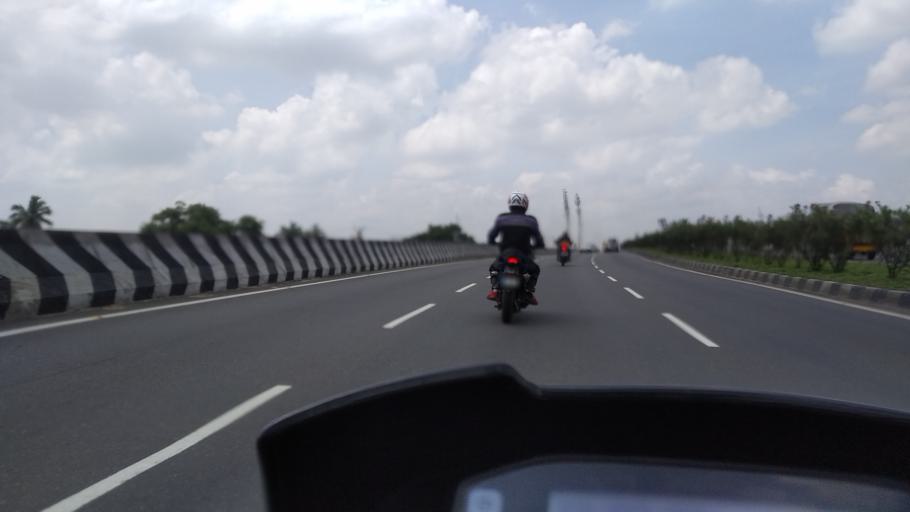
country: IN
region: Tamil Nadu
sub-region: Tiruppur
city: Avinashi
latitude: 11.1264
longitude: 77.1971
